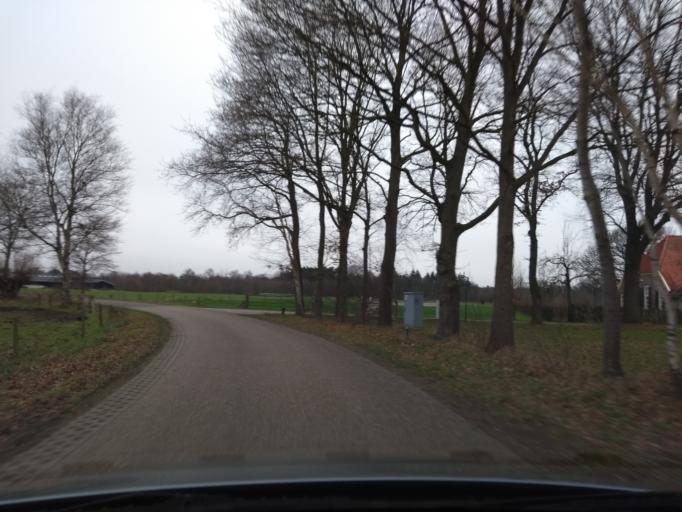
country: NL
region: Gelderland
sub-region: Gemeente Bronckhorst
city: Zelhem
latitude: 52.0661
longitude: 6.3888
